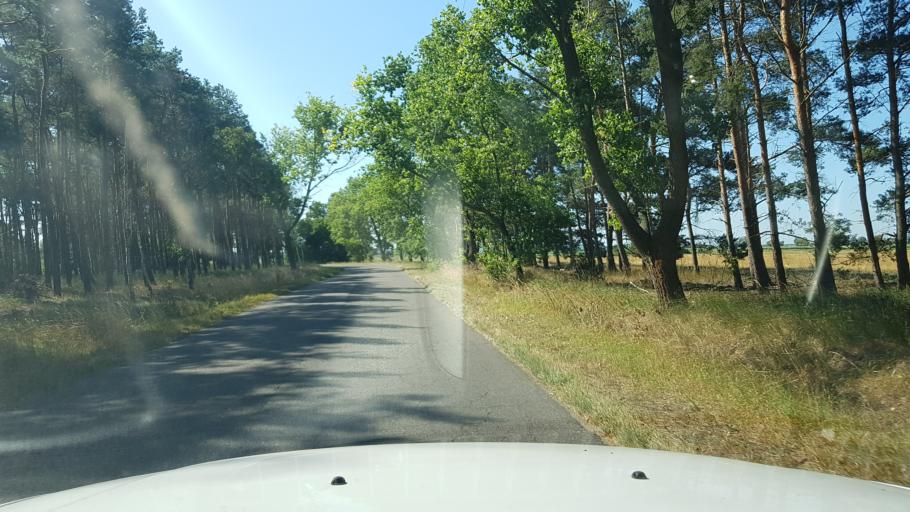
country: PL
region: West Pomeranian Voivodeship
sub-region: Powiat goleniowski
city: Goleniow
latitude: 53.4805
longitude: 14.7106
